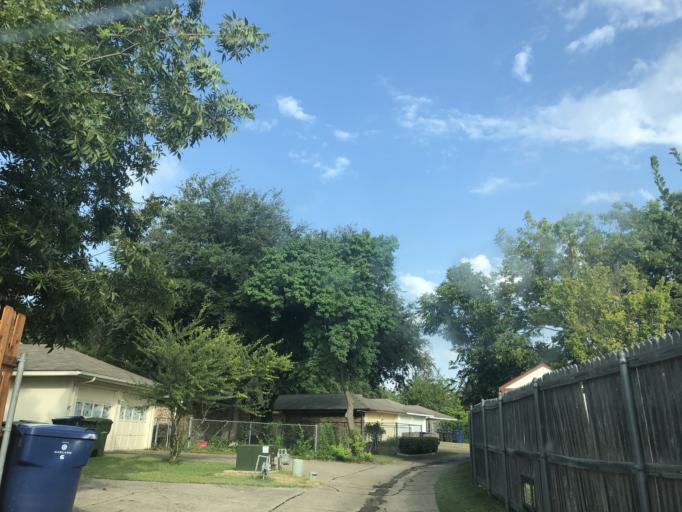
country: US
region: Texas
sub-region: Dallas County
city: Garland
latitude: 32.8577
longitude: -96.6241
